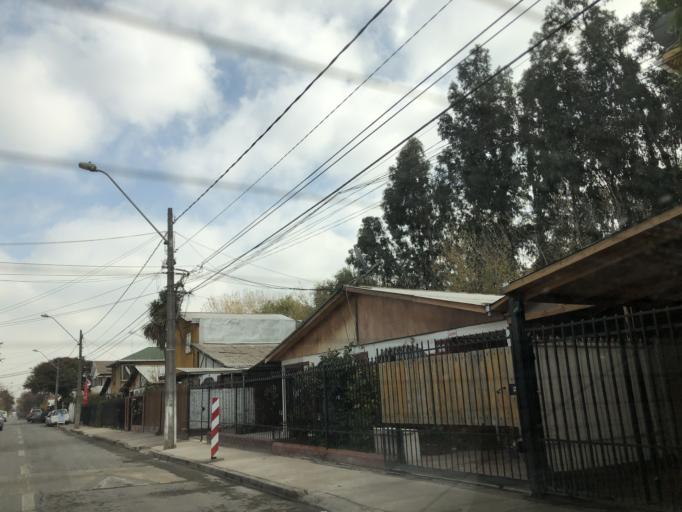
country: CL
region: Santiago Metropolitan
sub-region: Provincia de Cordillera
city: Puente Alto
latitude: -33.5772
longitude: -70.5890
